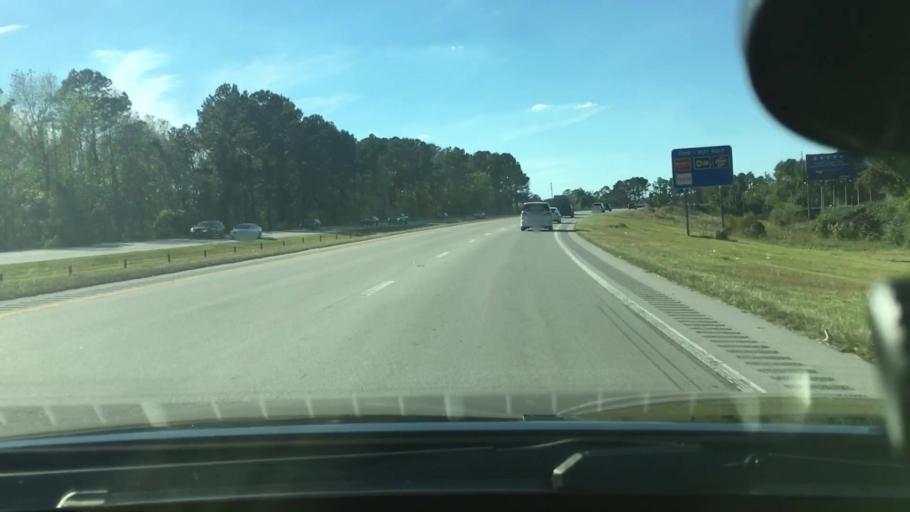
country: US
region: North Carolina
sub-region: Craven County
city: Trent Woods
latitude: 35.0996
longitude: -77.0749
